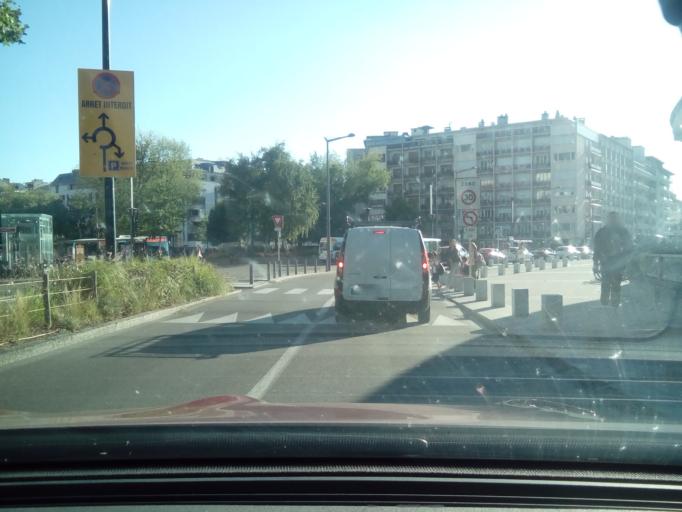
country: FR
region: Rhone-Alpes
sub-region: Departement de la Haute-Savoie
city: Annecy
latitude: 45.9020
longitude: 6.1222
